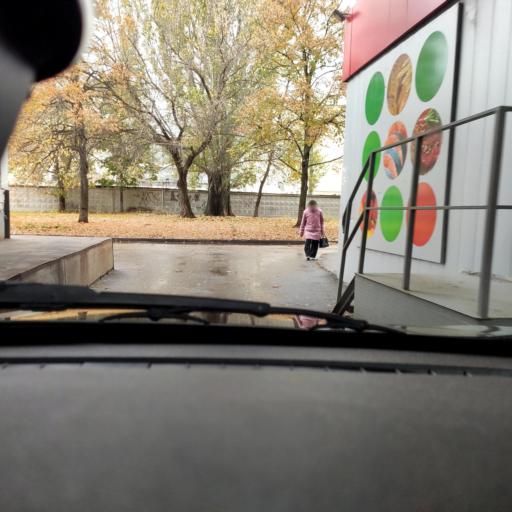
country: RU
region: Samara
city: Tol'yatti
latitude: 53.5029
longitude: 49.4023
